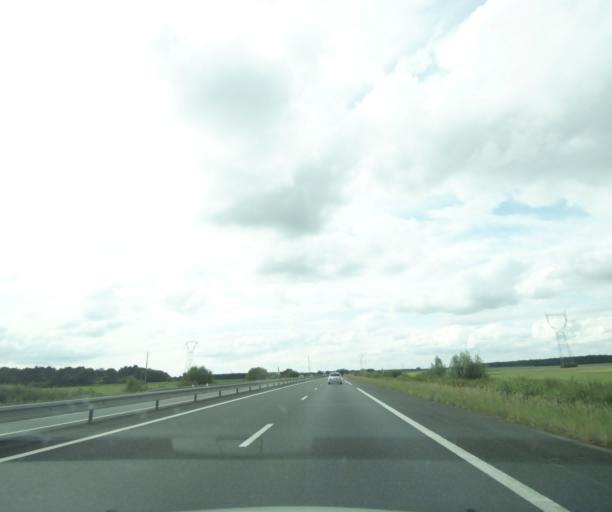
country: FR
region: Centre
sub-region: Departement du Cher
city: La Chapelle-Saint-Ursin
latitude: 47.0655
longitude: 2.2924
